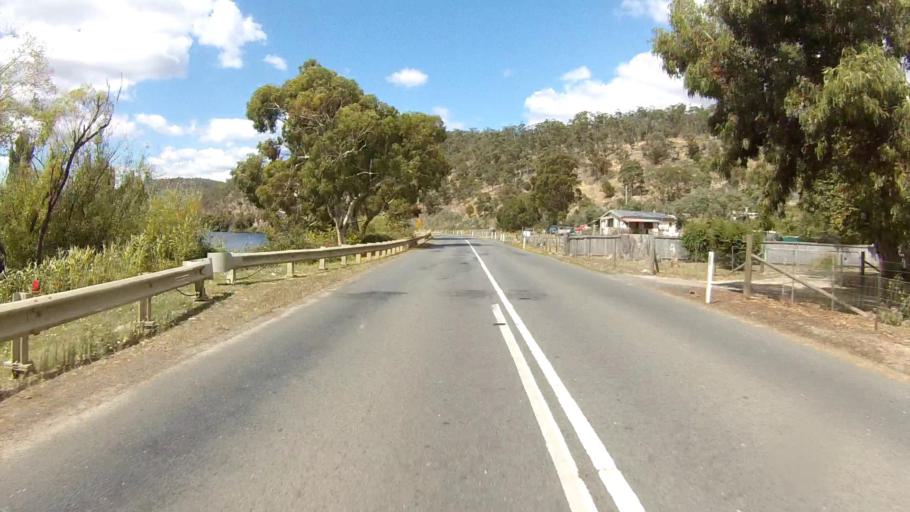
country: AU
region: Tasmania
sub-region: Derwent Valley
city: New Norfolk
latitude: -42.7758
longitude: 147.0281
